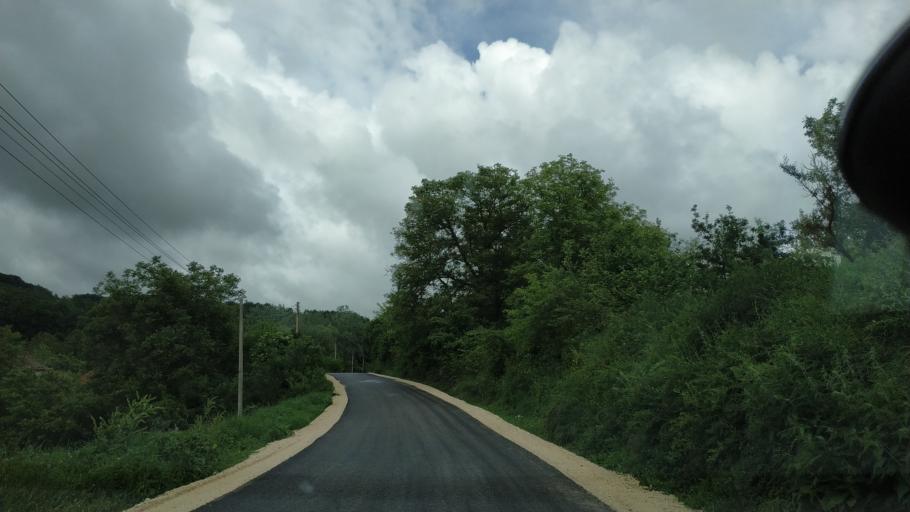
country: RS
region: Central Serbia
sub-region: Zajecarski Okrug
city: Soko Banja
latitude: 43.6724
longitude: 21.9136
